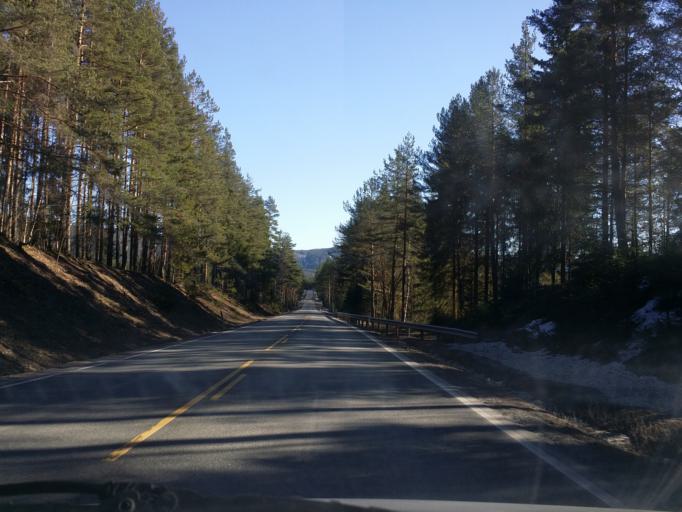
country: NO
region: Buskerud
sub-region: Ringerike
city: Honefoss
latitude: 60.3049
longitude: 10.1655
